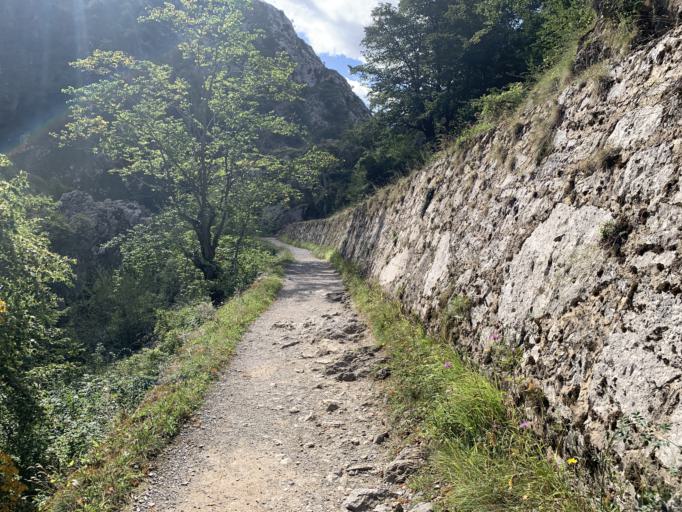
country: ES
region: Castille and Leon
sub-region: Provincia de Leon
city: Posada de Valdeon
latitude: 43.2295
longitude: -4.8942
